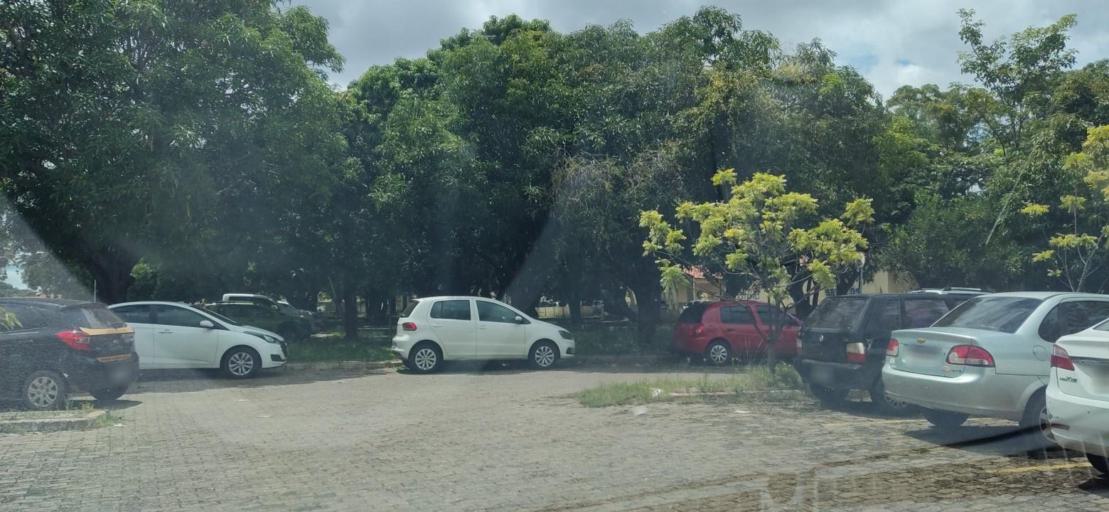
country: BR
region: Maranhao
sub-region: Timon
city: Timon
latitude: -5.0760
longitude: -42.8277
